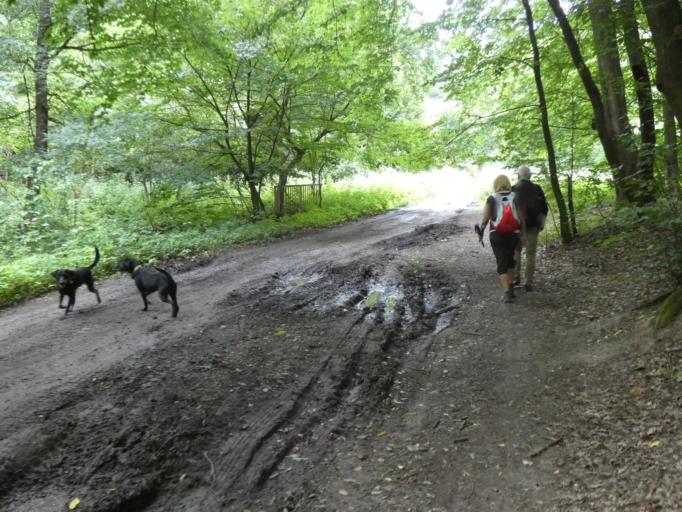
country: HU
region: Pest
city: Szob
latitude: 47.8417
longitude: 18.8930
